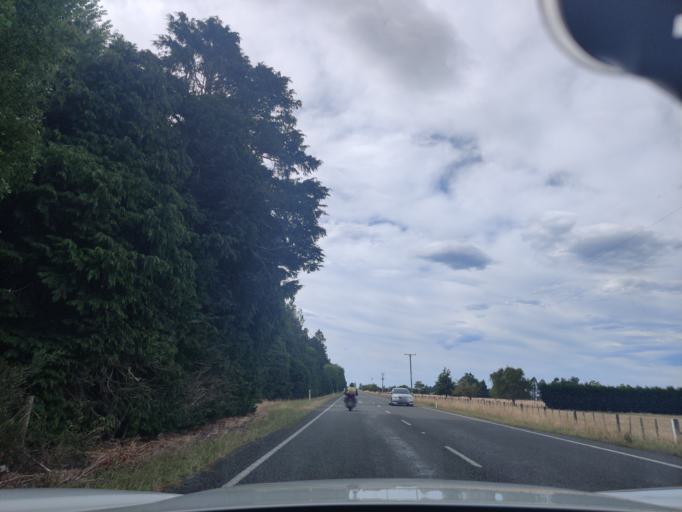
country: NZ
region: Wellington
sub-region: Masterton District
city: Masterton
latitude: -40.8666
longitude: 175.6453
